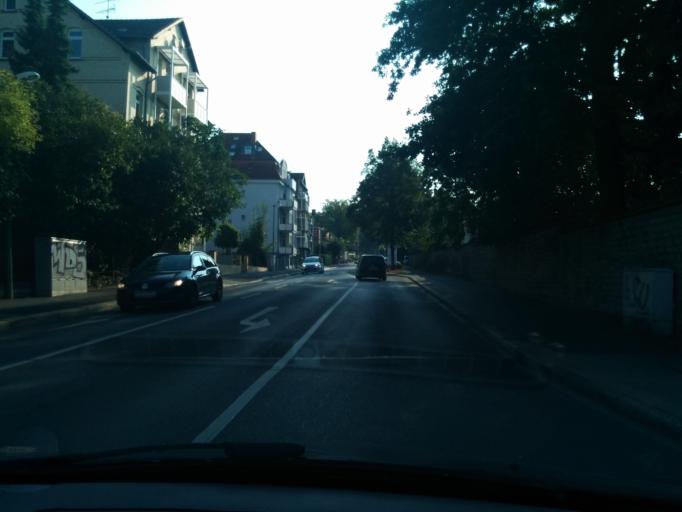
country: DE
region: Lower Saxony
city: Goettingen
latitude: 51.5271
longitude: 9.9467
